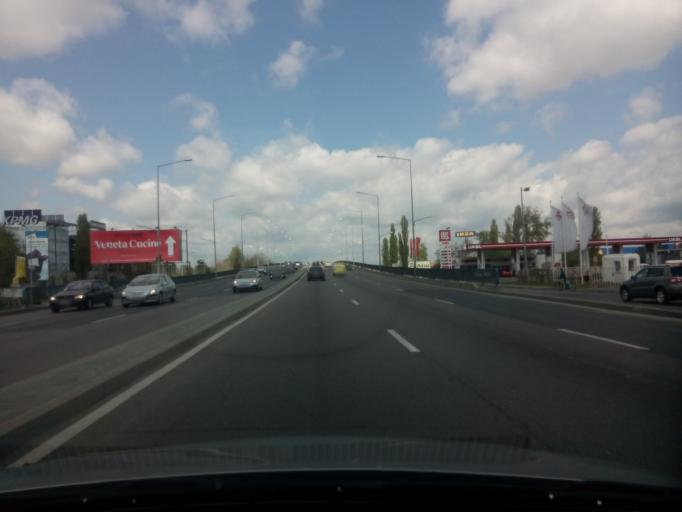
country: RO
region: Ilfov
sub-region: Comuna Otopeni
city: Otopeni
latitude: 44.5014
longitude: 26.0803
